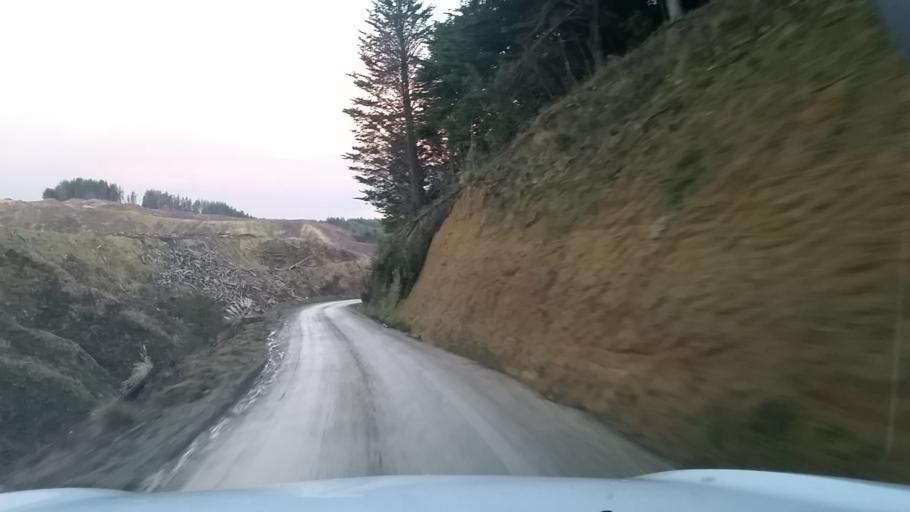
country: NZ
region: Manawatu-Wanganui
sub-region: Wanganui District
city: Wanganui
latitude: -39.7523
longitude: 174.8884
